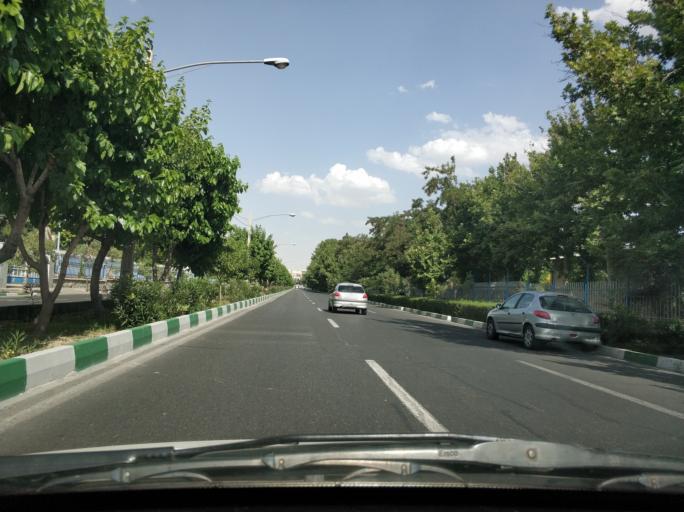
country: IR
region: Tehran
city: Tajrish
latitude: 35.7439
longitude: 51.5795
